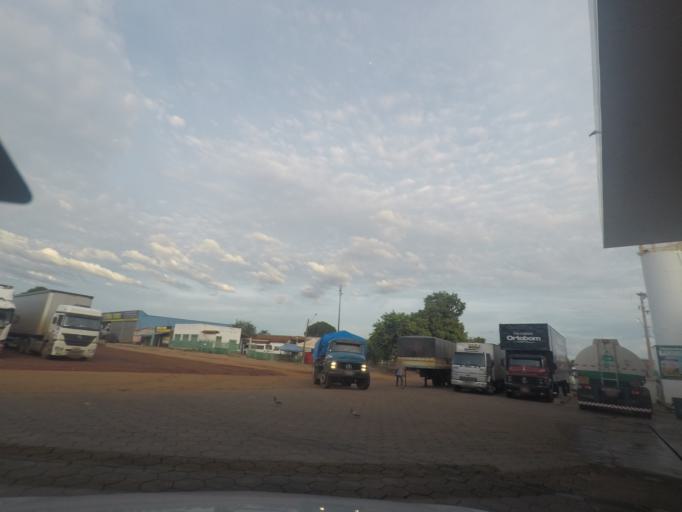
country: BR
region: Goias
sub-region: Trindade
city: Trindade
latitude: -16.7225
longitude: -49.3811
